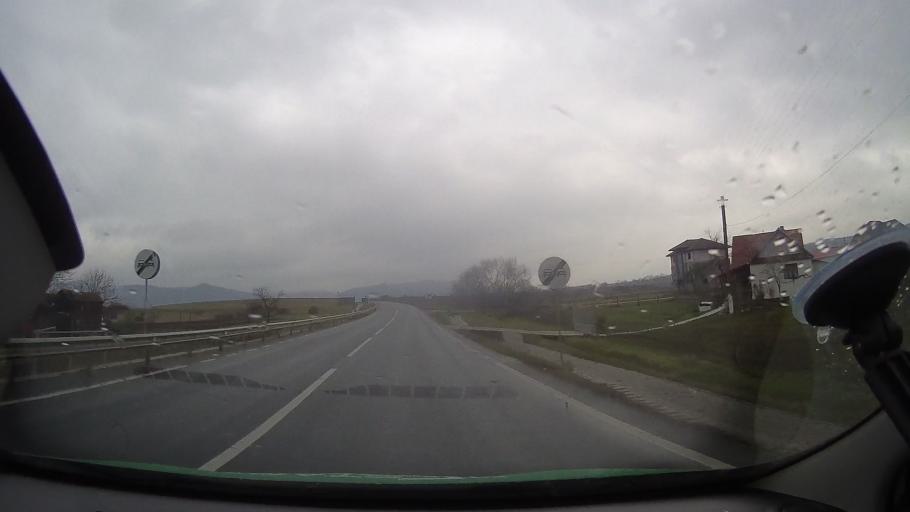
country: RO
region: Hunedoara
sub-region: Comuna Baia de Cris
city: Baia de Cris
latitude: 46.1684
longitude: 22.7387
